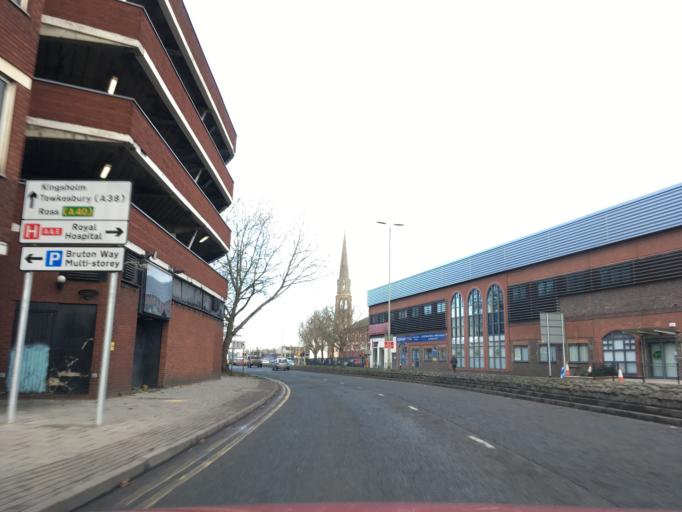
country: GB
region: England
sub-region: Gloucestershire
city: Gloucester
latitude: 51.8657
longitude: -2.2401
